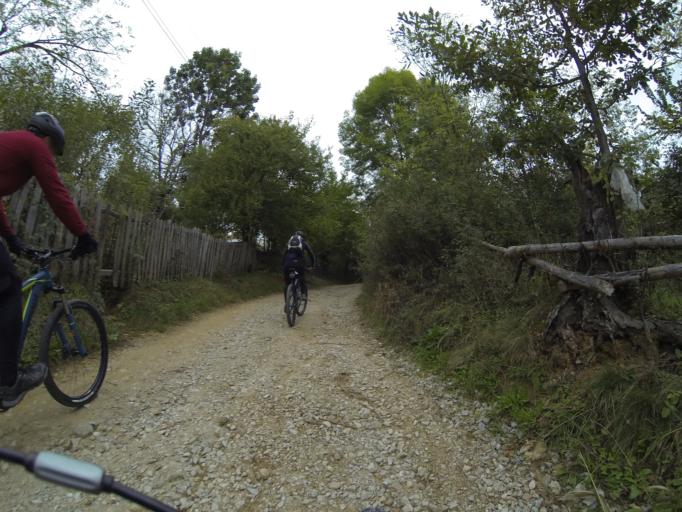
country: RO
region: Gorj
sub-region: Comuna Tismana
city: Sohodol
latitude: 45.0543
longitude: 22.8952
